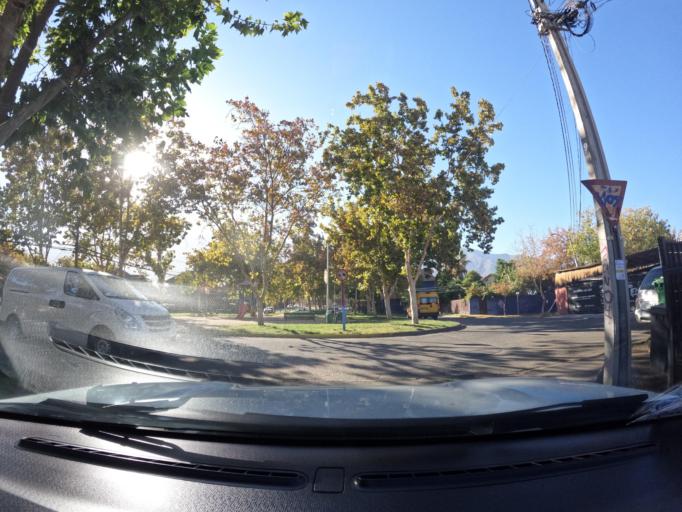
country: CL
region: Santiago Metropolitan
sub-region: Provincia de Santiago
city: Villa Presidente Frei, Nunoa, Santiago, Chile
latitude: -33.4755
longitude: -70.5518
